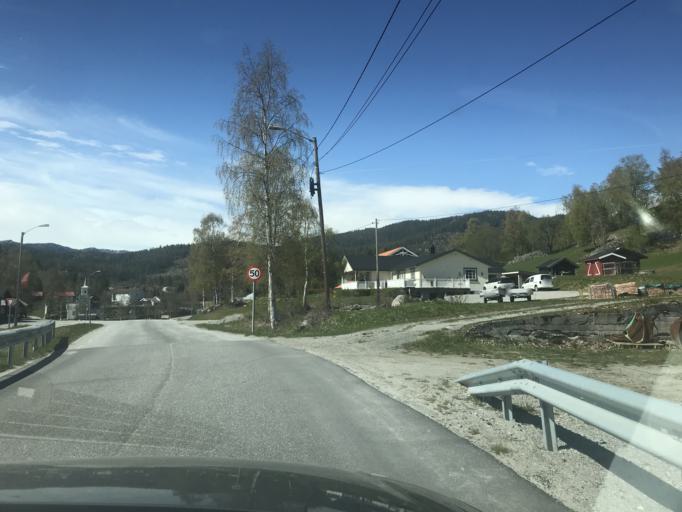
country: NO
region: Telemark
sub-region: Hjartdal
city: Sauland
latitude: 59.7549
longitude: 8.7939
